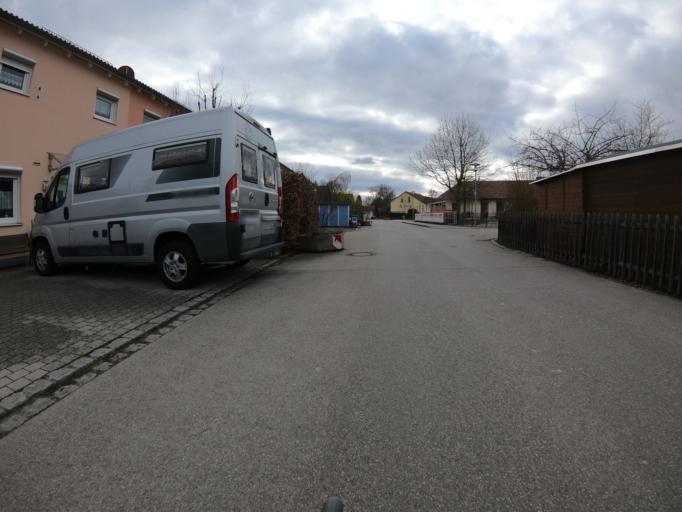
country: DE
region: Bavaria
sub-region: Upper Bavaria
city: Fuerstenfeldbruck
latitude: 48.1878
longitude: 11.2578
